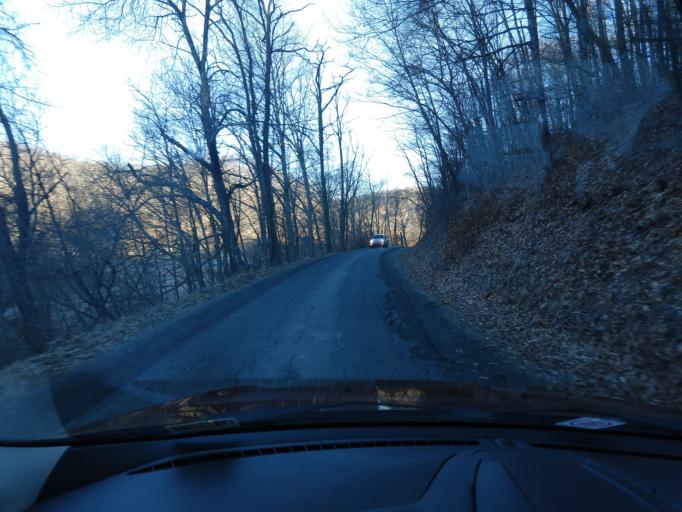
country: US
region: West Virginia
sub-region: Greenbrier County
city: Rainelle
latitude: 37.8922
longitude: -80.7312
